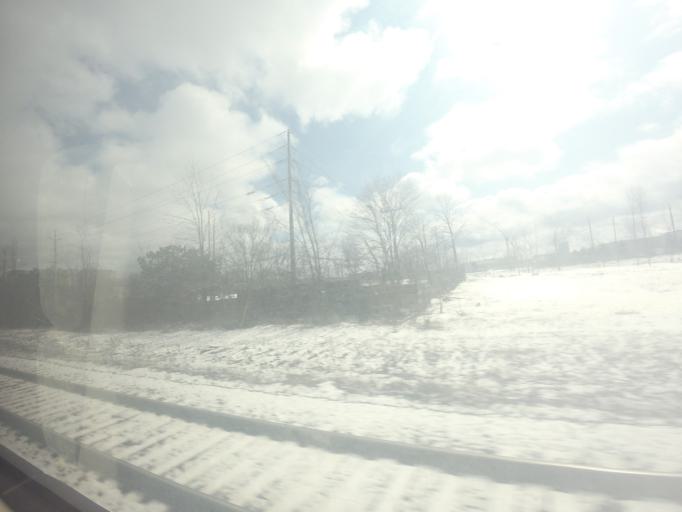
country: CA
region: Ontario
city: Ajax
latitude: 43.8511
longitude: -79.0276
